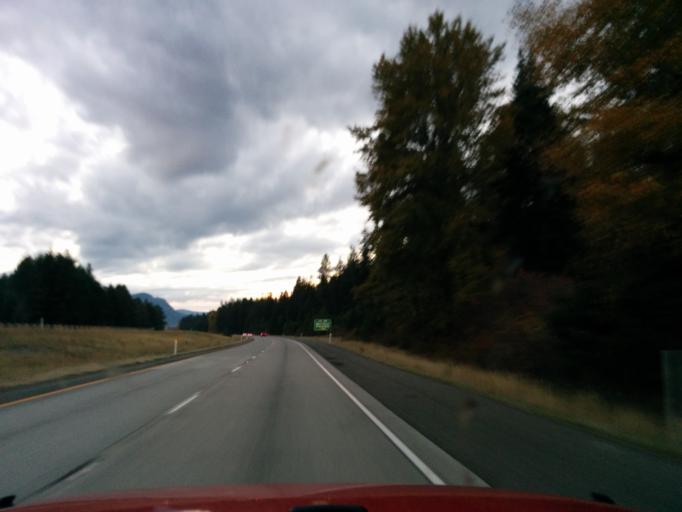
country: US
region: Washington
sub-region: Kittitas County
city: Cle Elum
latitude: 47.2125
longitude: -121.1038
